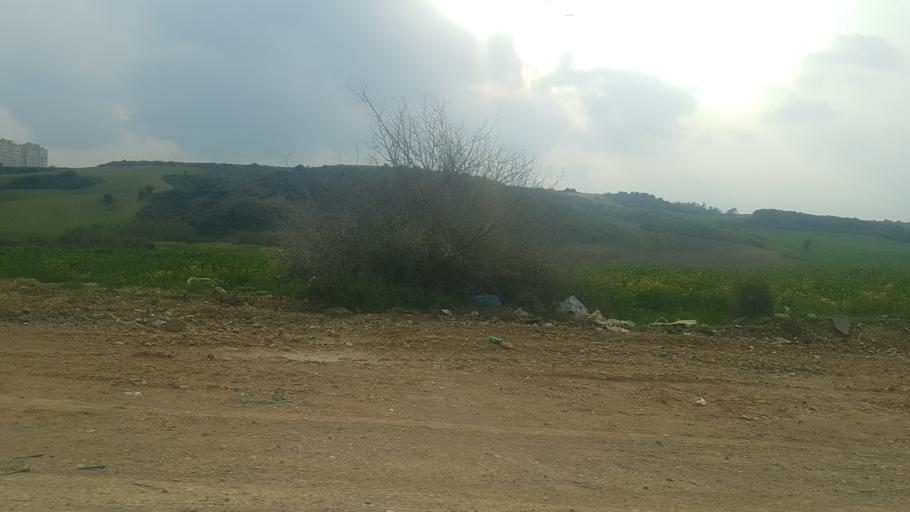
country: TR
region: Adana
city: Seyhan
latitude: 37.0422
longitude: 35.2135
